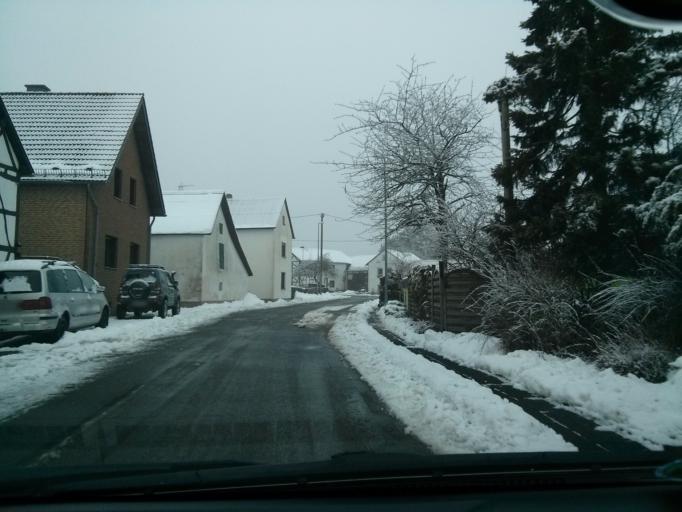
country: DE
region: Rheinland-Pfalz
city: Kirchsahr
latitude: 50.5081
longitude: 6.8445
